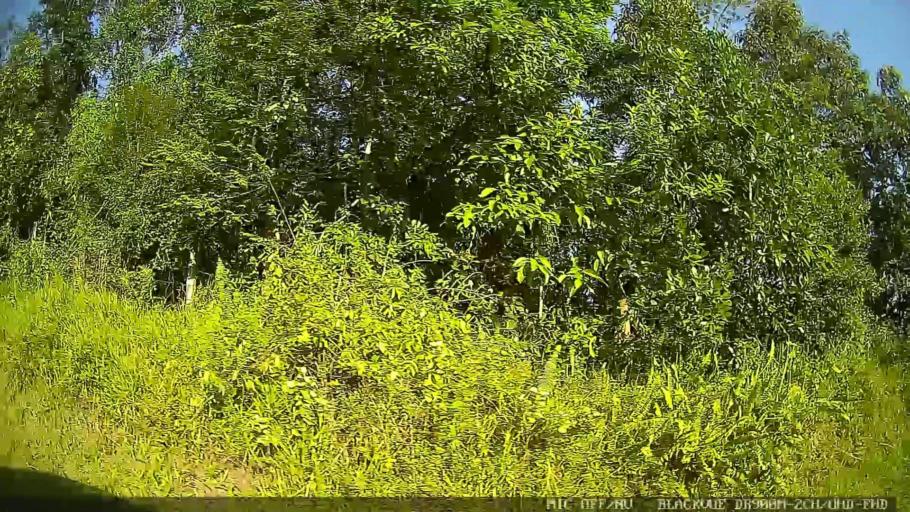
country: BR
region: Sao Paulo
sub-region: Itanhaem
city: Itanhaem
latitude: -24.1517
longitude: -46.8213
